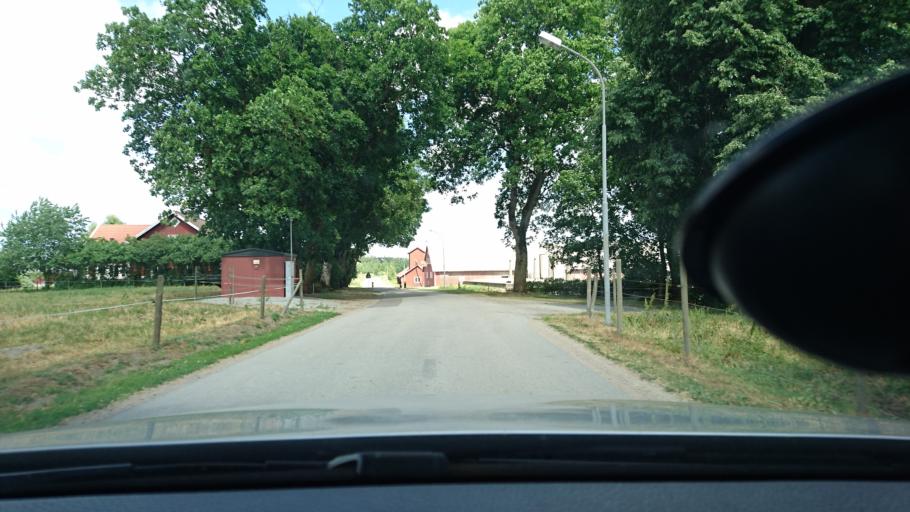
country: SE
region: Kronoberg
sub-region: Alvesta Kommun
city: Moheda
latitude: 56.9499
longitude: 14.5711
